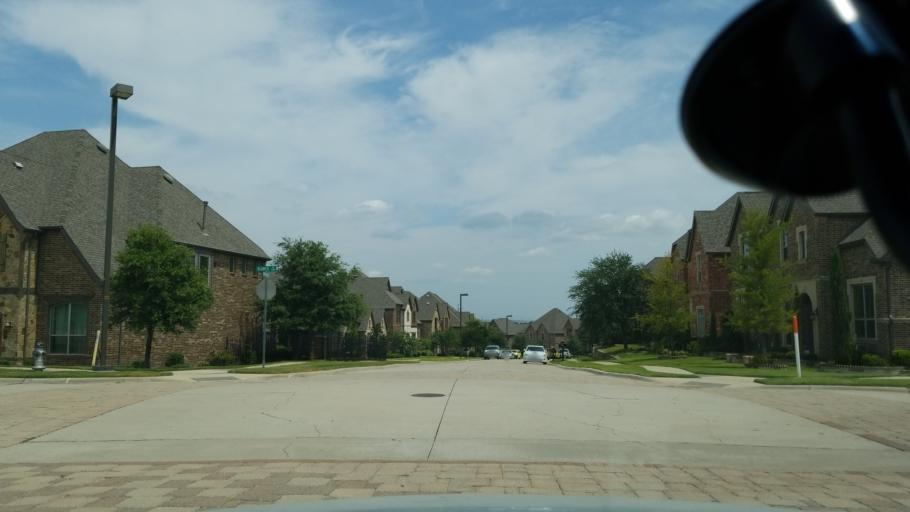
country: US
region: Texas
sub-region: Dallas County
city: Farmers Branch
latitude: 32.9070
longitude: -96.9481
